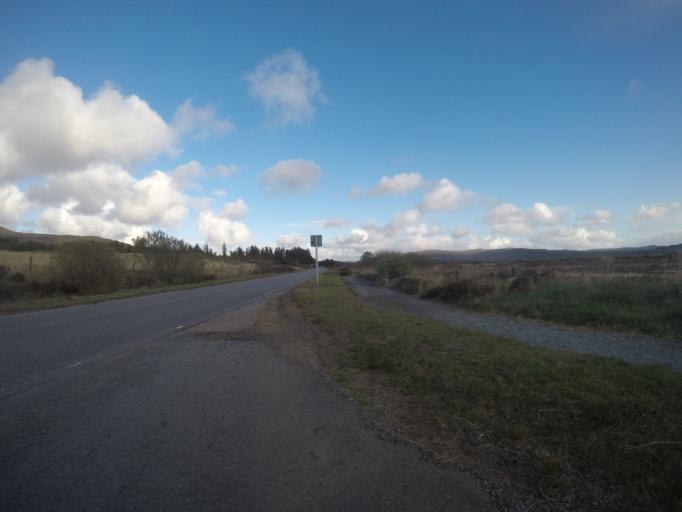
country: GB
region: Scotland
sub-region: Highland
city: Portree
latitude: 57.4552
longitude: -6.2705
